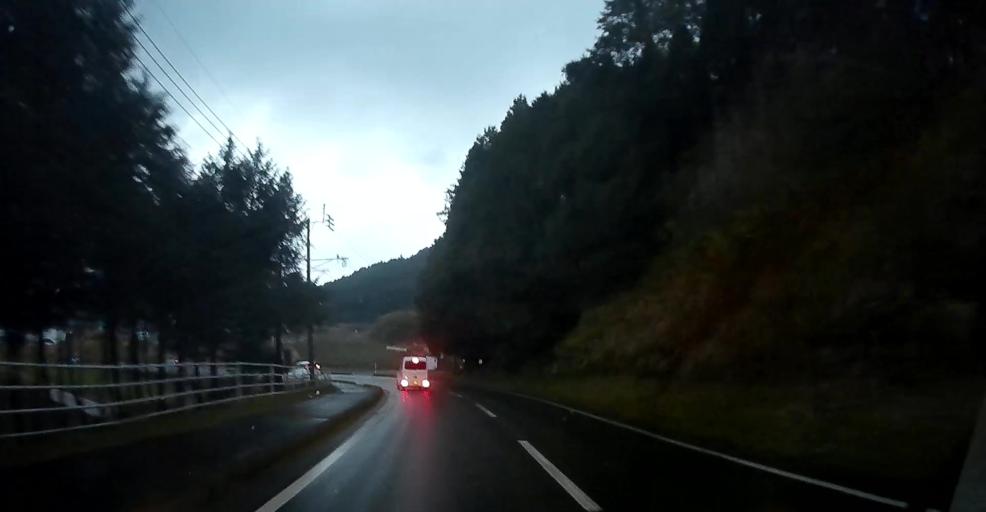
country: JP
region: Kumamoto
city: Ozu
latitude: 32.8374
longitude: 130.9160
